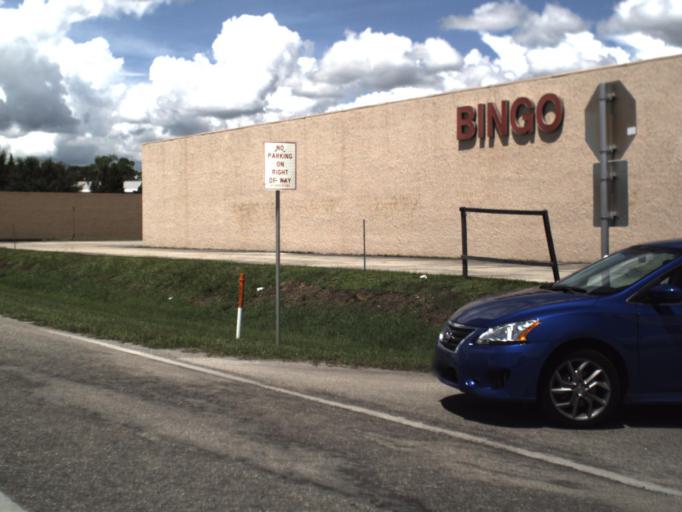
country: US
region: Florida
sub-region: Charlotte County
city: Port Charlotte
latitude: 26.9690
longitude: -82.0805
